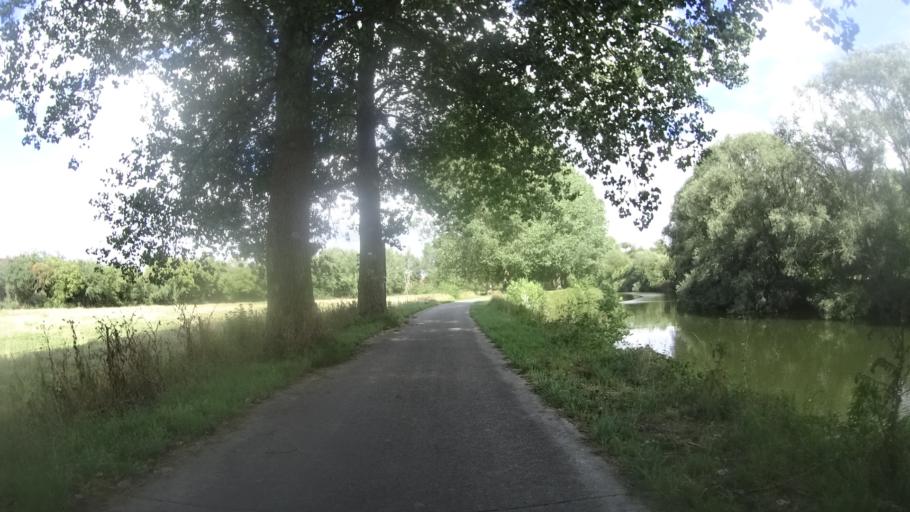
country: BE
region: Wallonia
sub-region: Province du Hainaut
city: Merbes-le-Chateau
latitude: 50.3172
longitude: 4.1997
